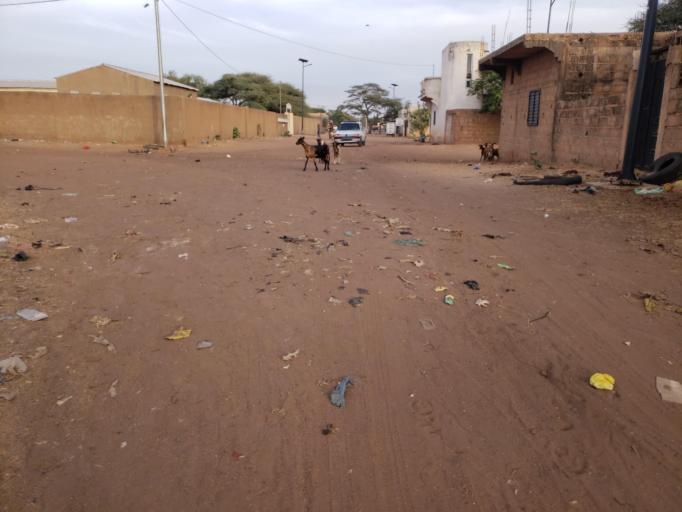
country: SN
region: Louga
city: Ndibene Dahra
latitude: 15.3918
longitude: -15.1147
